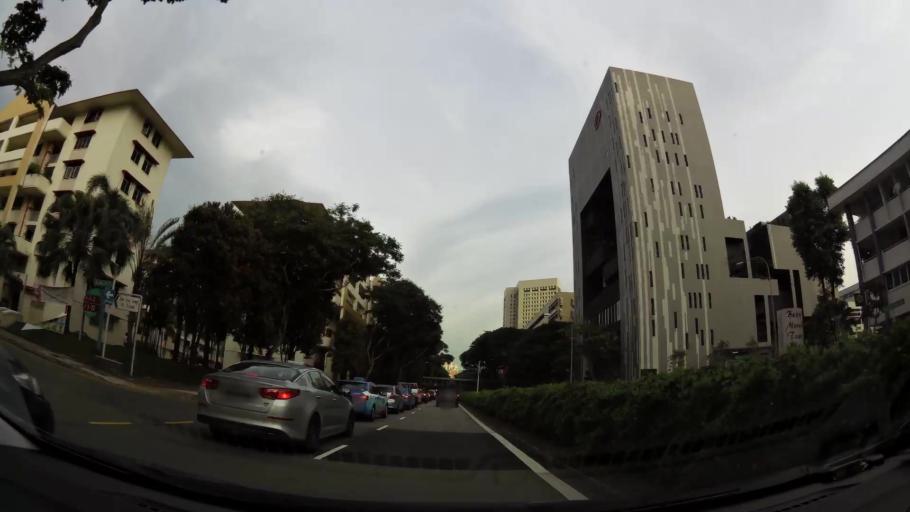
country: SG
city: Singapore
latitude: 1.2845
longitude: 103.8162
